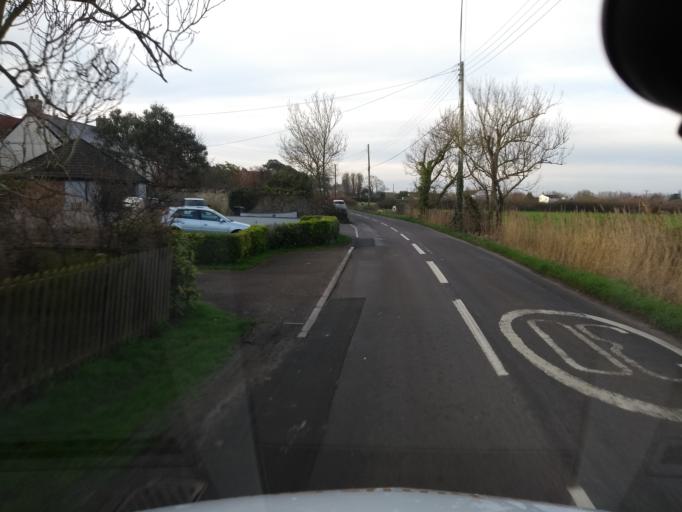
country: GB
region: England
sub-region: Somerset
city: Burnham-on-Sea
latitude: 51.2622
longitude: -2.9614
